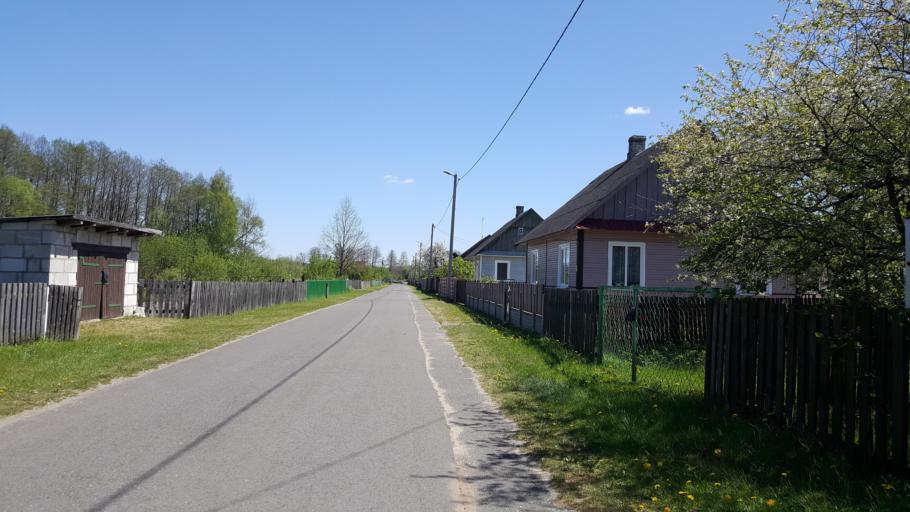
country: BY
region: Brest
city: Kamyanyuki
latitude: 52.5619
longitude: 23.8024
